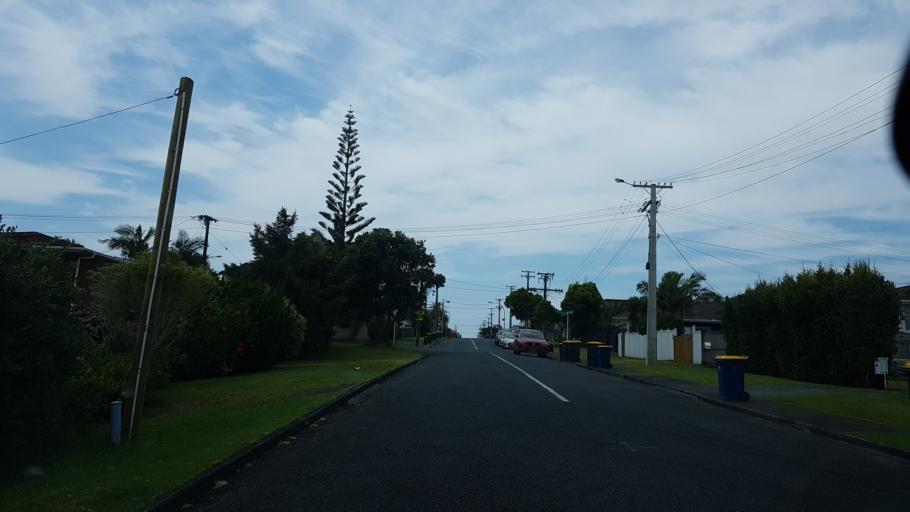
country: NZ
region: Auckland
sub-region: Auckland
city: North Shore
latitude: -36.8044
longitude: 174.7734
